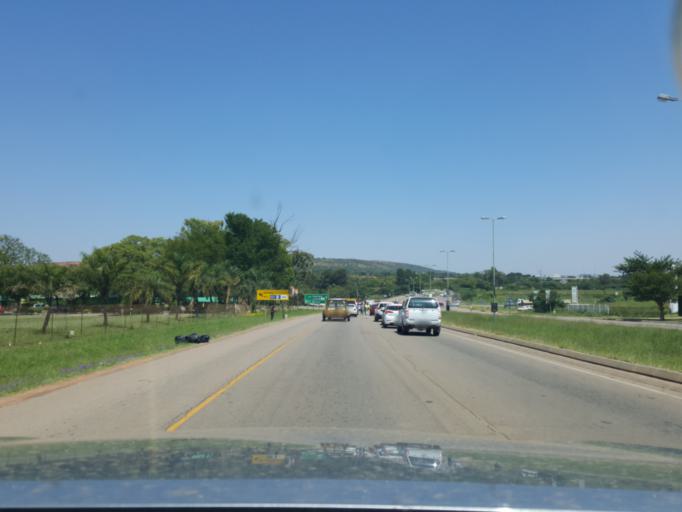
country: ZA
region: Gauteng
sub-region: City of Tshwane Metropolitan Municipality
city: Pretoria
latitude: -25.6852
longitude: 28.2953
